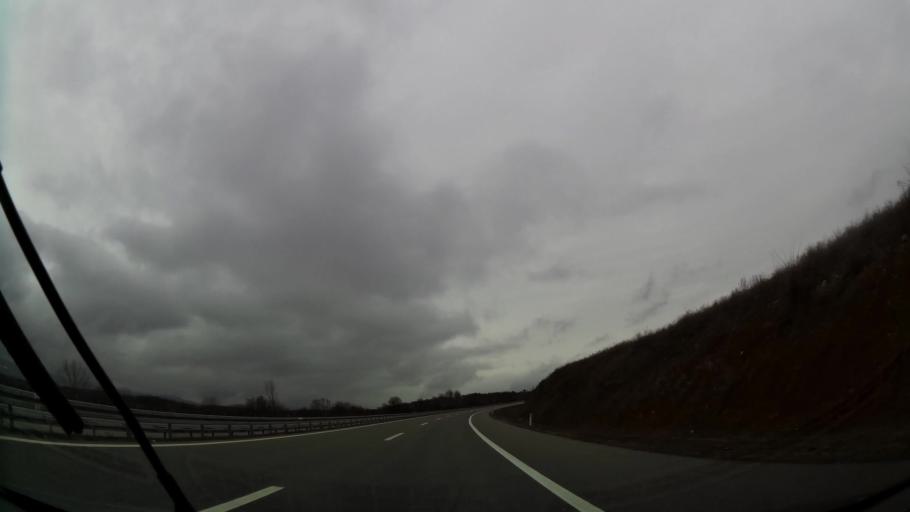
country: RS
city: Miratovac
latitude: 42.2632
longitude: 21.7001
